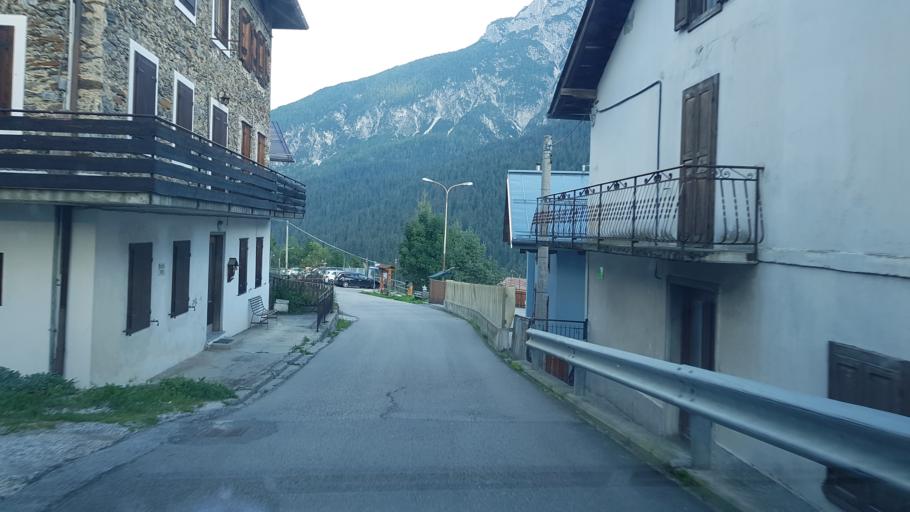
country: IT
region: Veneto
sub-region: Provincia di Belluno
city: San Pietro di Cadore
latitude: 46.5726
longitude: 12.5868
